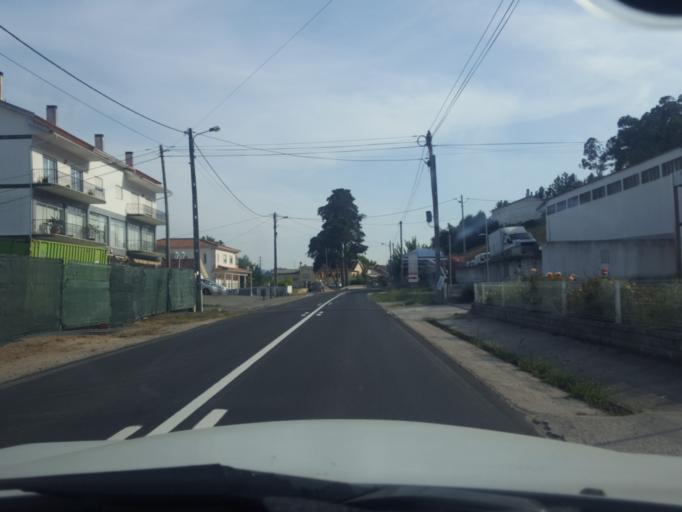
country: PT
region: Leiria
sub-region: Leiria
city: Leiria
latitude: 39.7143
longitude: -8.7889
